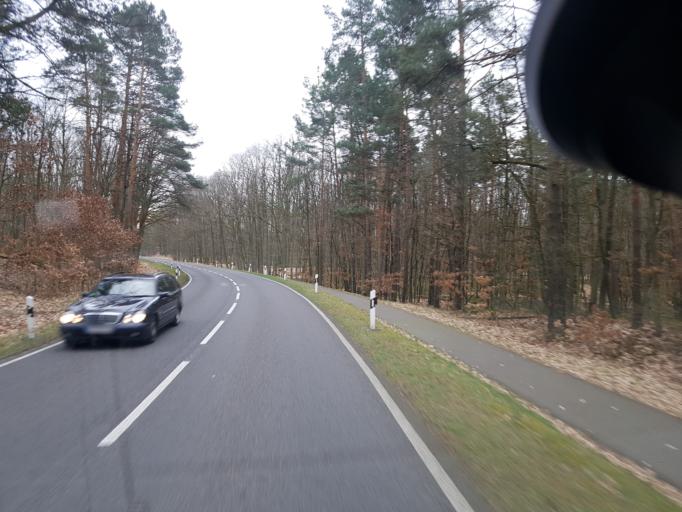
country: DE
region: Brandenburg
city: Gross Lindow
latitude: 52.1750
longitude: 14.4822
